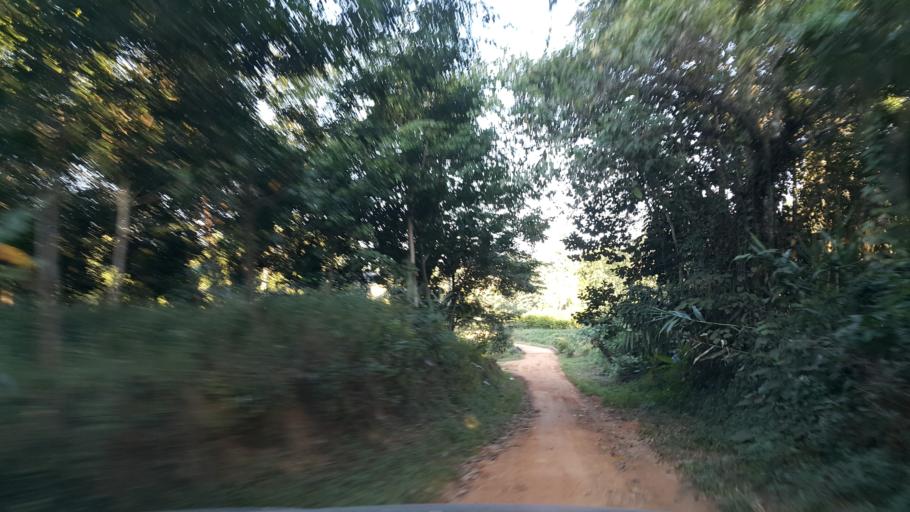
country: TH
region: Sukhothai
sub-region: Amphoe Si Satchanalai
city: Si Satchanalai
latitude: 17.5873
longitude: 99.6131
